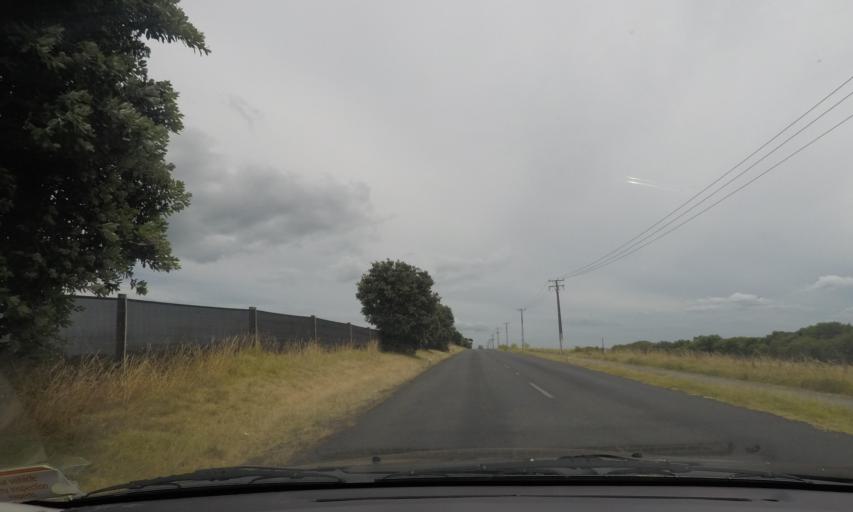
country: NZ
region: Auckland
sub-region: Auckland
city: Mangere
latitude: -36.9745
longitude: 174.7688
